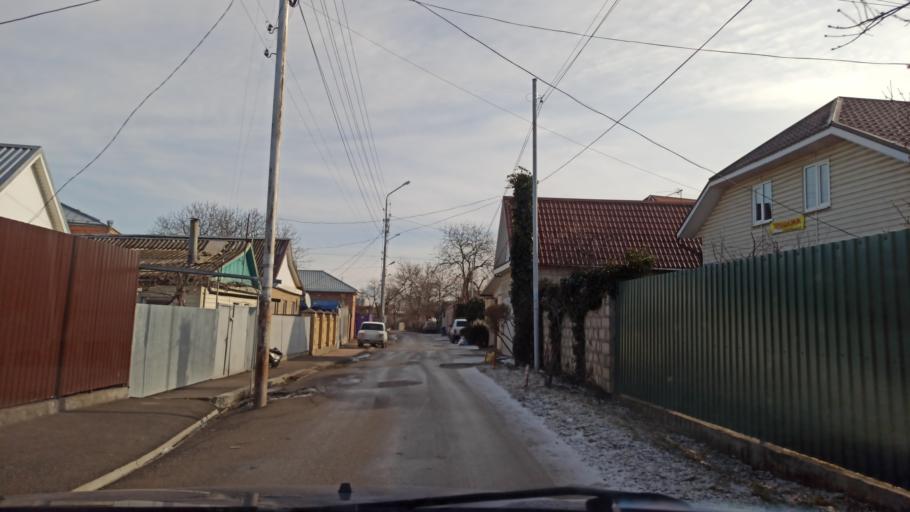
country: RU
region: Stavropol'skiy
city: Yessentukskaya
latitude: 44.0394
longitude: 42.8815
